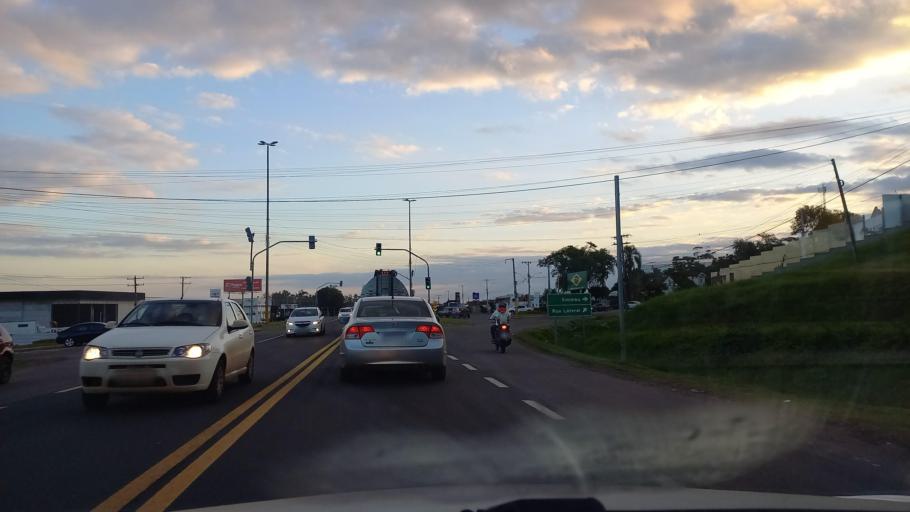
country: BR
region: Rio Grande do Sul
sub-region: Santa Cruz Do Sul
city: Santa Cruz do Sul
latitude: -29.6862
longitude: -52.4453
